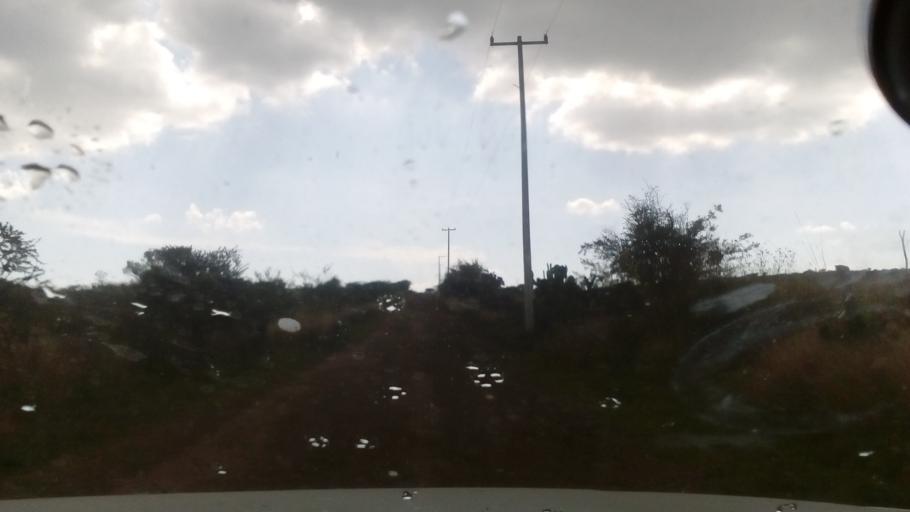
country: MX
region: Guanajuato
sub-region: Silao de la Victoria
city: San Francisco (Banos de Agua Caliente)
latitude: 21.1657
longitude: -101.4172
